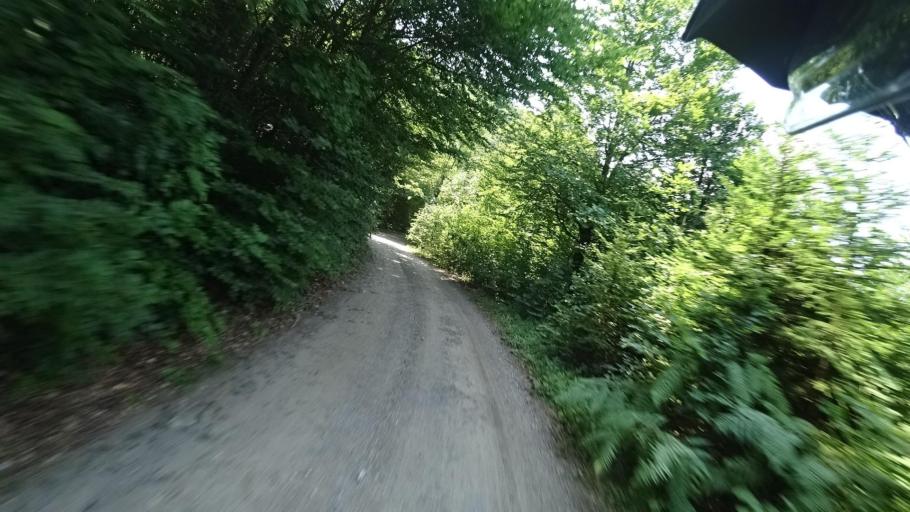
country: HR
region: Primorsko-Goranska
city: Vrbovsko
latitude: 45.3078
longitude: 15.1447
